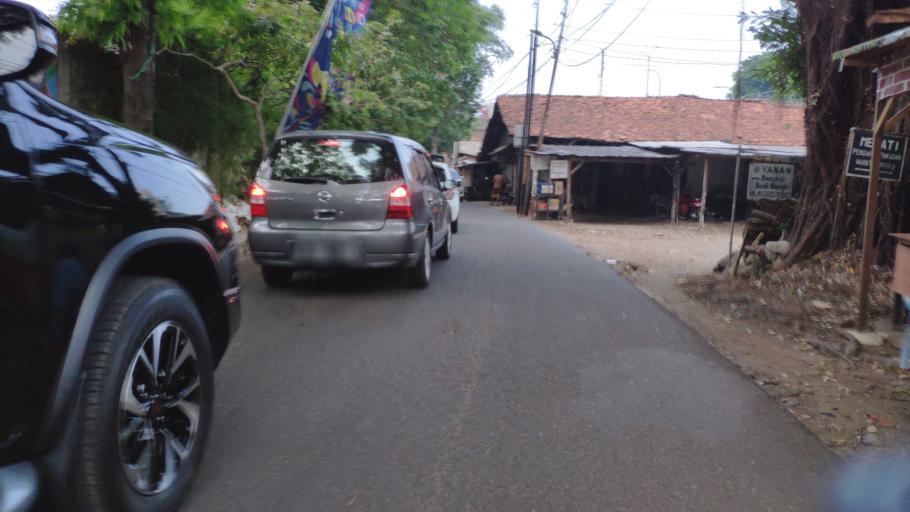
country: ID
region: West Java
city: Pamulang
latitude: -6.2932
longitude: 106.7986
